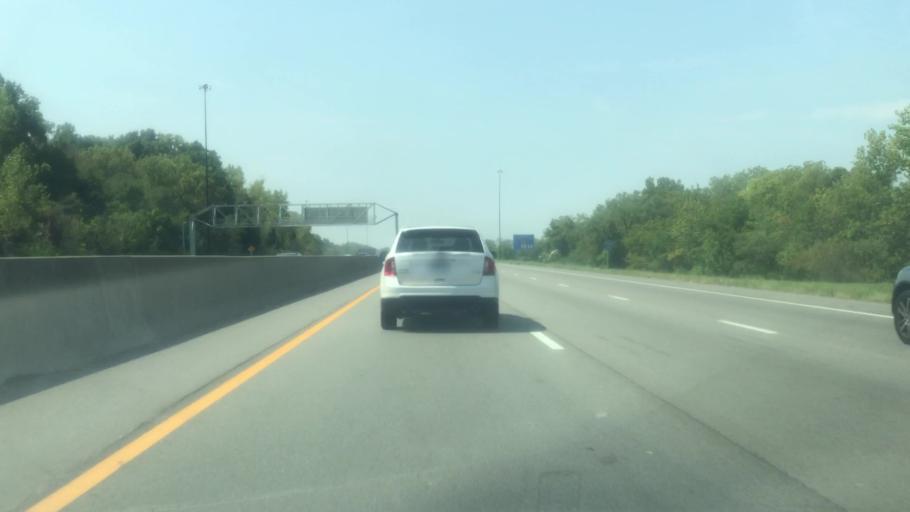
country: US
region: Kansas
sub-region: Johnson County
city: Roeland Park
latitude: 39.0540
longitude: -94.6339
